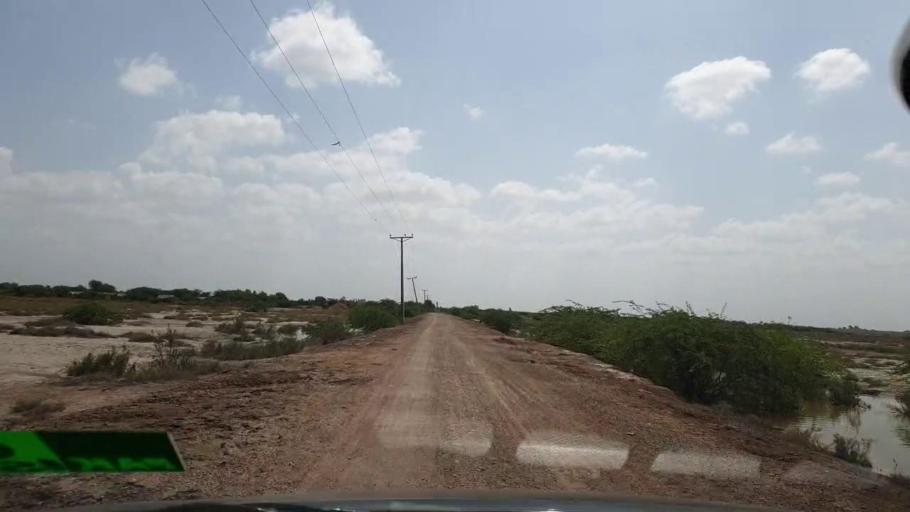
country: PK
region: Sindh
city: Kadhan
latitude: 24.6012
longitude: 69.1852
